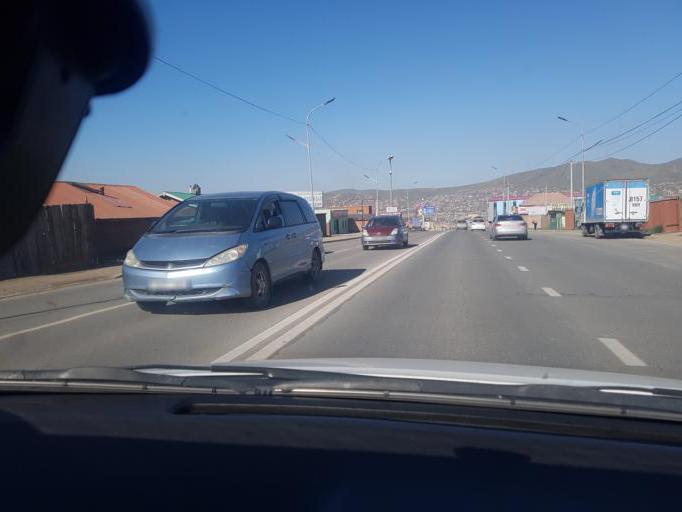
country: MN
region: Ulaanbaatar
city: Ulaanbaatar
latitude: 47.9555
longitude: 106.8344
